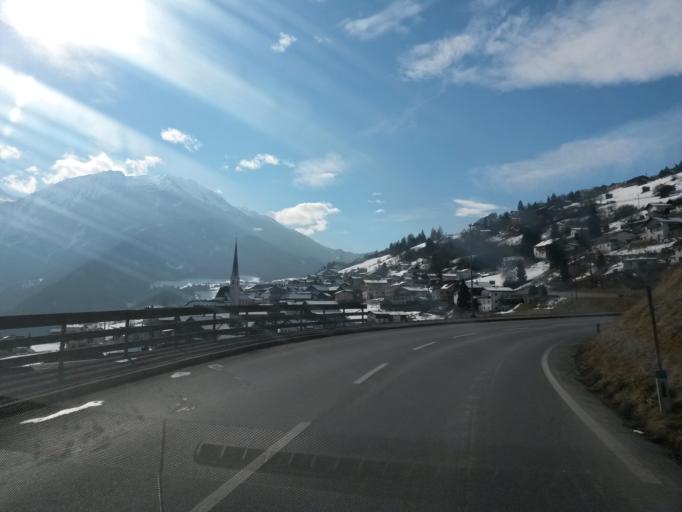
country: AT
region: Tyrol
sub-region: Politischer Bezirk Imst
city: Wenns
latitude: 47.1743
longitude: 10.7336
